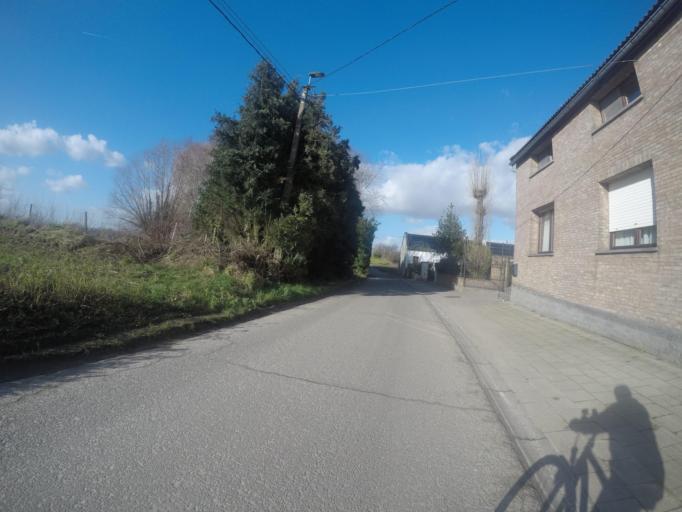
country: BE
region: Wallonia
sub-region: Province du Brabant Wallon
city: Rebecq-Rognon
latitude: 50.6810
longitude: 4.1485
